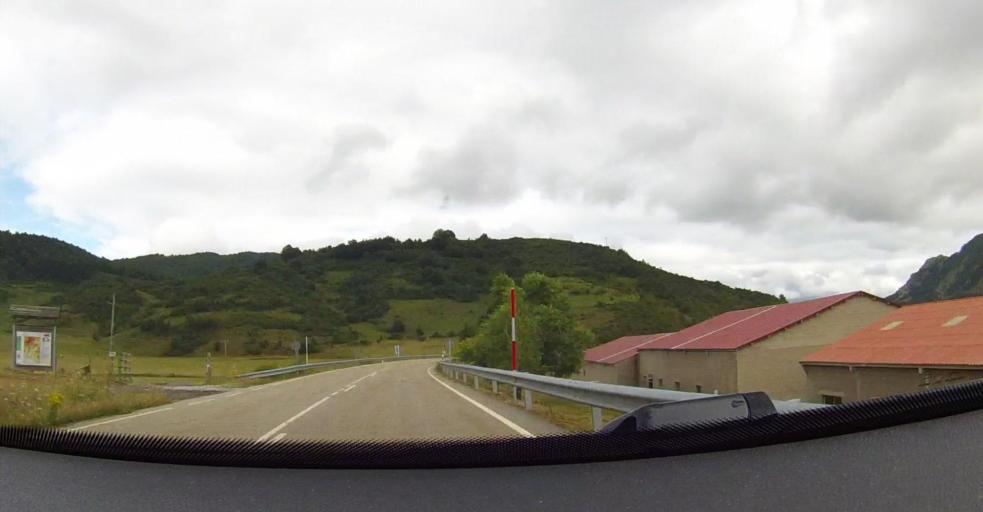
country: ES
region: Castille and Leon
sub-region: Provincia de Leon
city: Buron
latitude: 43.0257
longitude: -5.0487
